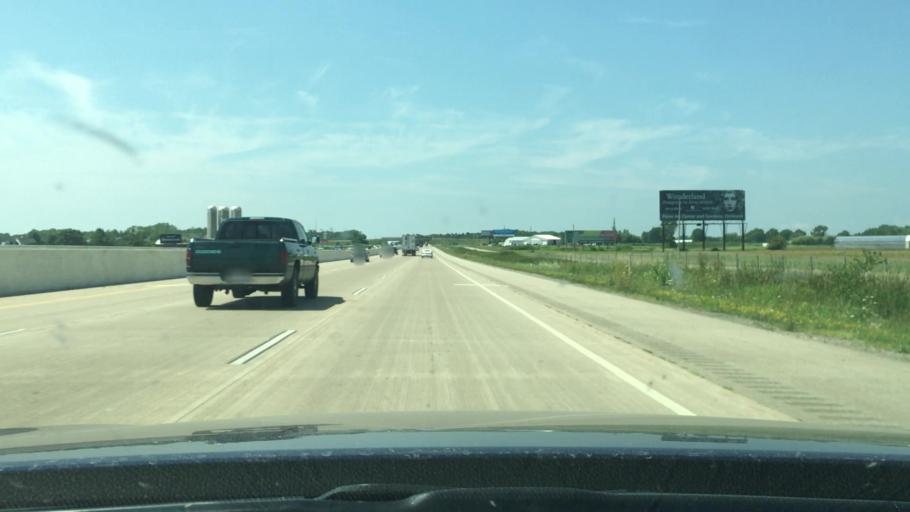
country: US
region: Wisconsin
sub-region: Winnebago County
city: Neenah
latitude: 44.1180
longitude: -88.5110
